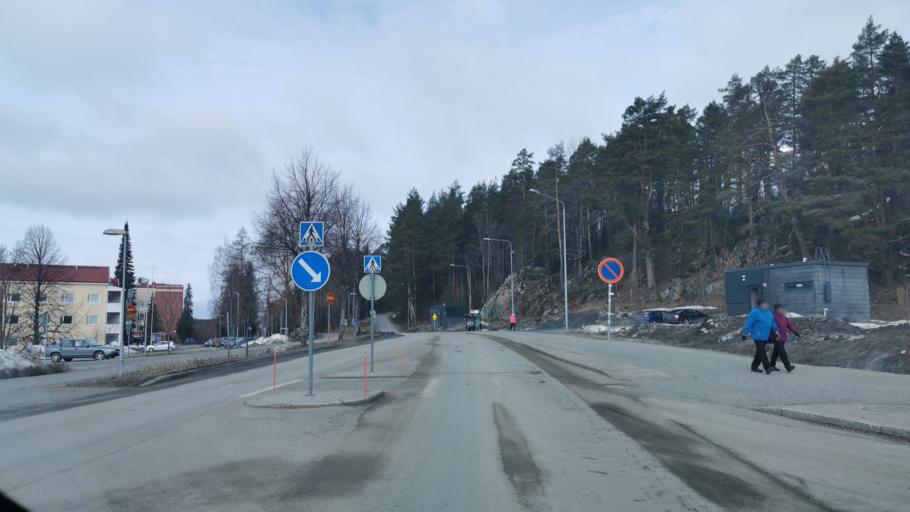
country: FI
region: Northern Savo
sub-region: Kuopio
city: Kuopio
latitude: 62.8970
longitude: 27.6417
